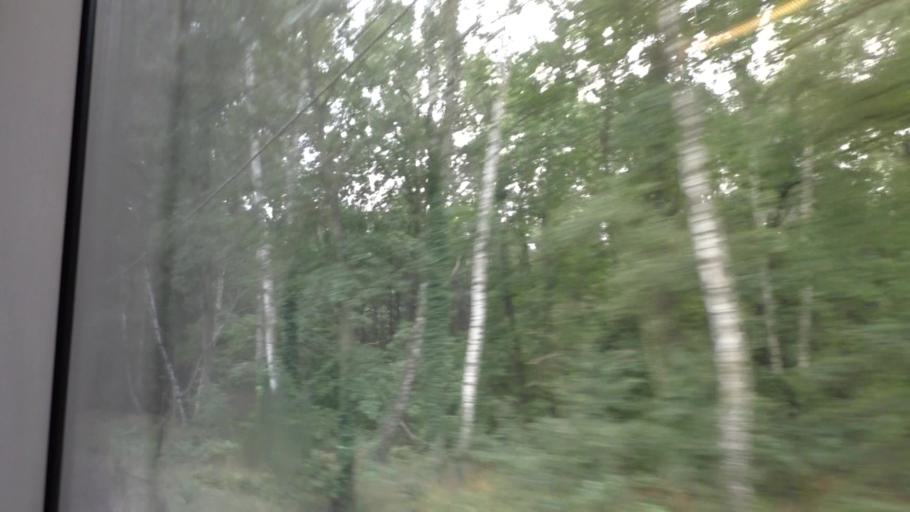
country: DE
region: Brandenburg
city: Storkow
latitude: 52.2684
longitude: 13.8877
